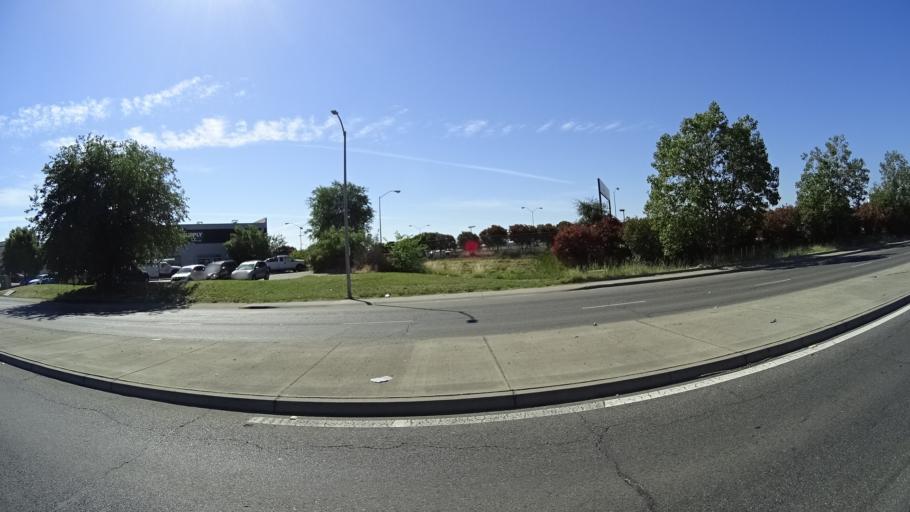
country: US
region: California
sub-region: Sacramento County
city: North Highlands
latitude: 38.6503
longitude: -121.3923
